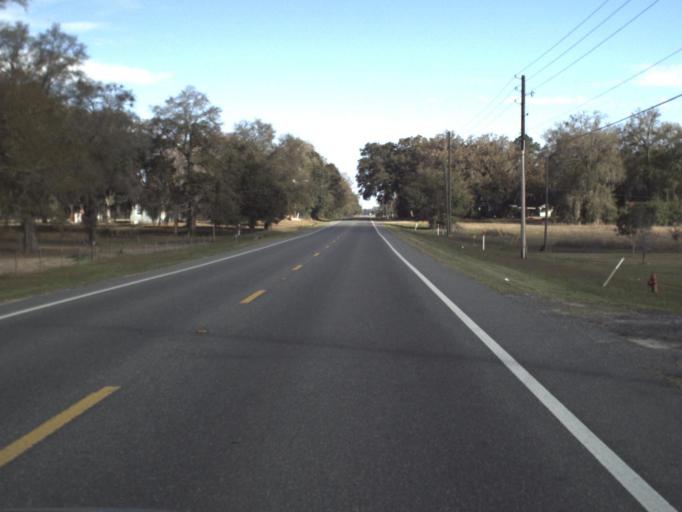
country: US
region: Florida
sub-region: Jackson County
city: Malone
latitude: 30.8897
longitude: -85.1612
